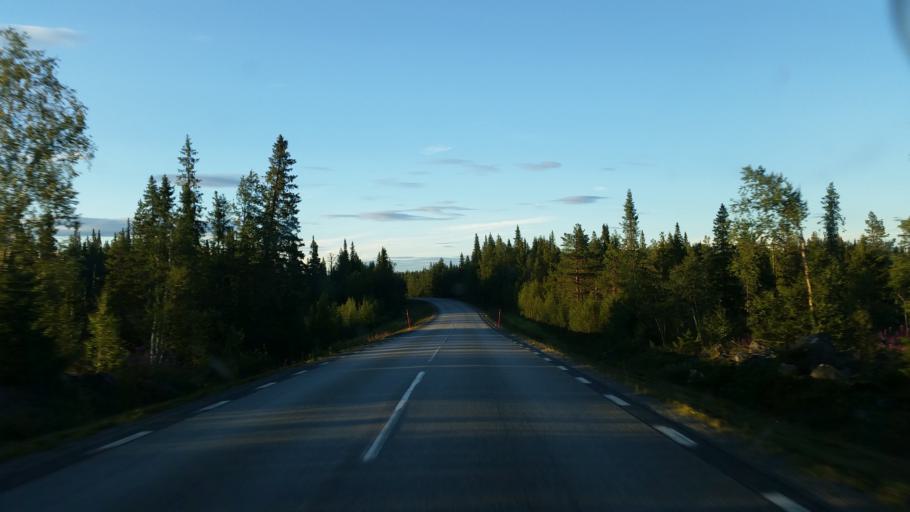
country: SE
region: Vaesterbotten
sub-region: Storumans Kommun
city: Storuman
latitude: 64.8900
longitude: 16.9854
